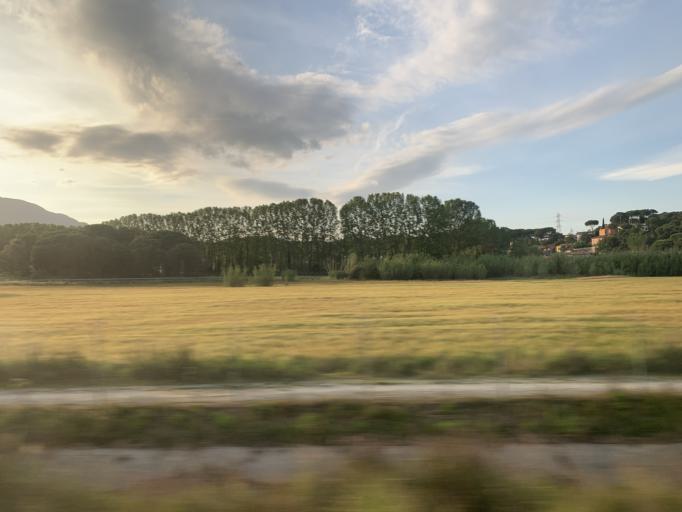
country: ES
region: Catalonia
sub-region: Provincia de Girona
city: Breda
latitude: 41.7255
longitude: 2.5637
